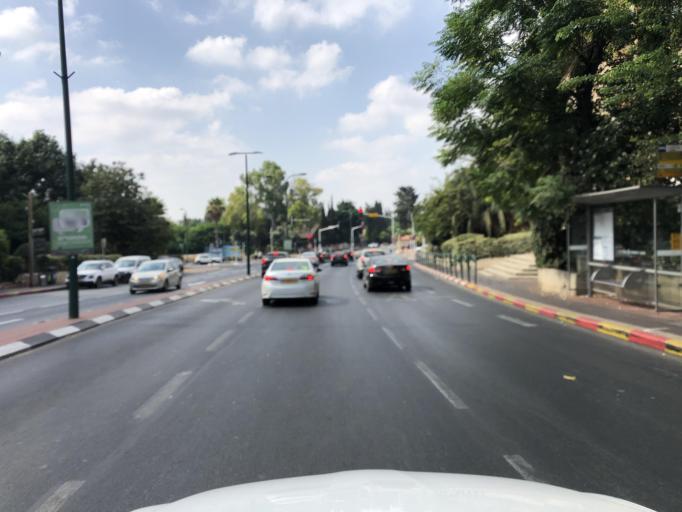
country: IL
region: Tel Aviv
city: Giv`atayim
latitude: 32.0598
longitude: 34.8282
